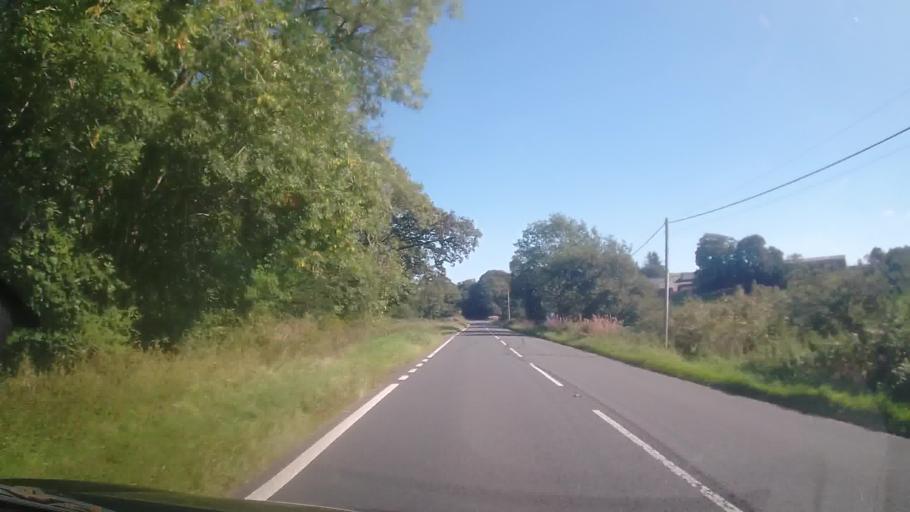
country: GB
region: Wales
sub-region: Sir Powys
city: Mochdre
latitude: 52.4806
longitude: -3.3374
